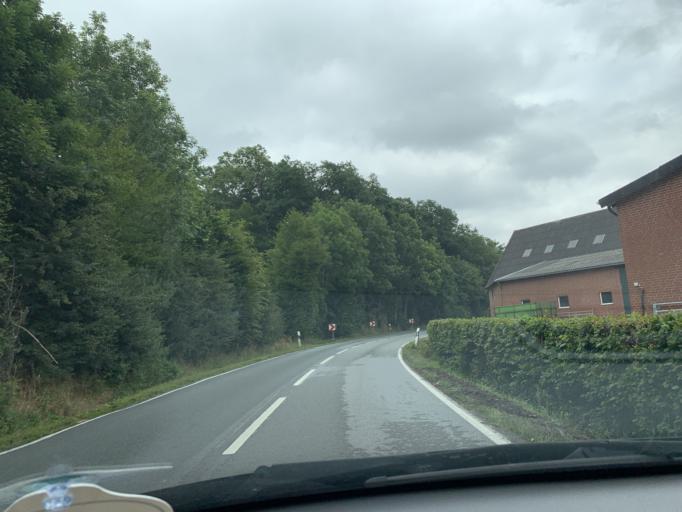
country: DE
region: North Rhine-Westphalia
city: Oelde
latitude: 51.8231
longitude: 8.0992
